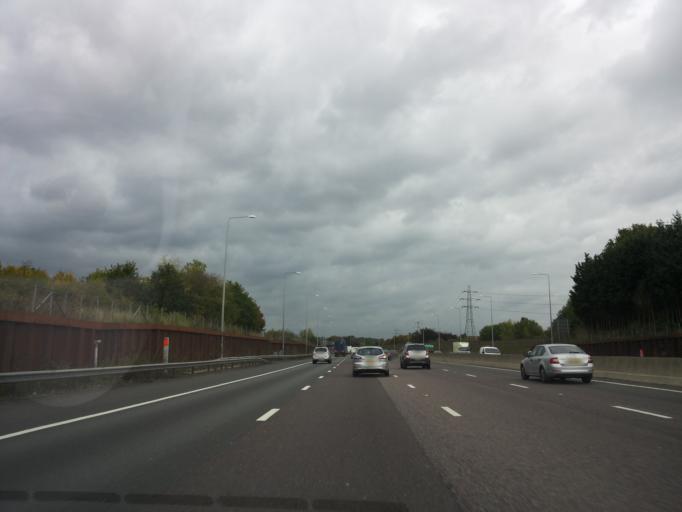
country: GB
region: England
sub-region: Hertfordshire
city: Radlett
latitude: 51.7106
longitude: -0.3055
